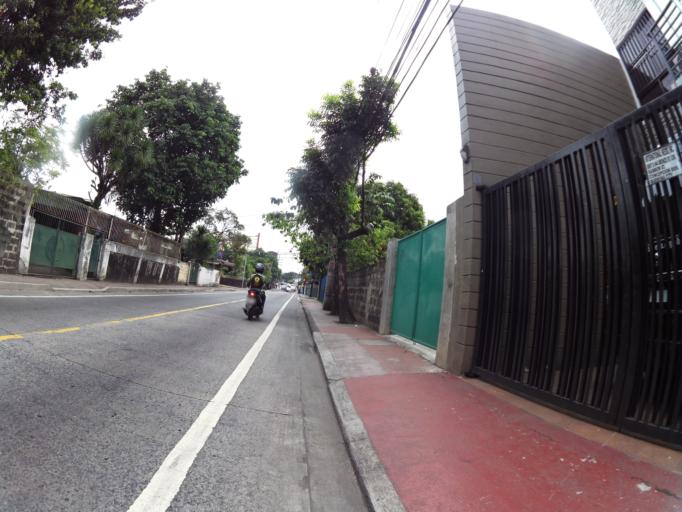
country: PH
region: Calabarzon
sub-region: Province of Rizal
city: Antipolo
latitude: 14.6407
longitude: 121.1160
